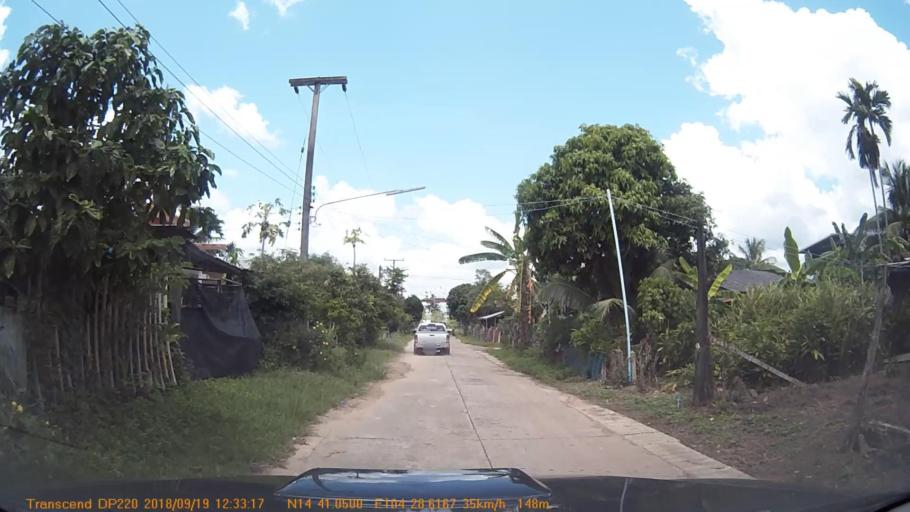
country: TH
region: Sisaket
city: Khun Han
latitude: 14.6843
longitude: 104.4769
